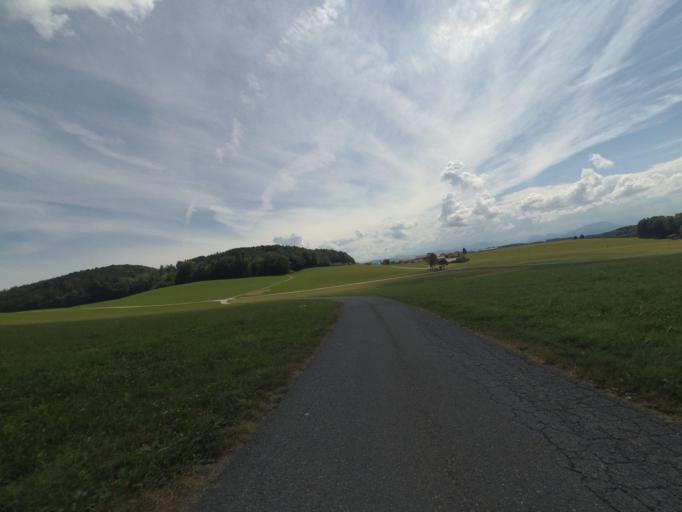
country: AT
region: Salzburg
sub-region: Politischer Bezirk Salzburg-Umgebung
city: Schleedorf
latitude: 47.9716
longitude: 13.1303
